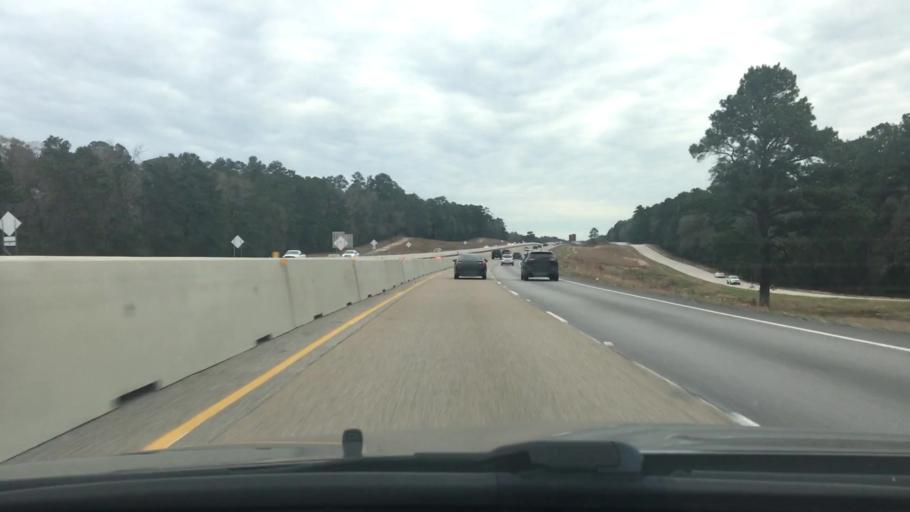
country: US
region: Texas
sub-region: Walker County
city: Huntsville
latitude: 30.6591
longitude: -95.5108
